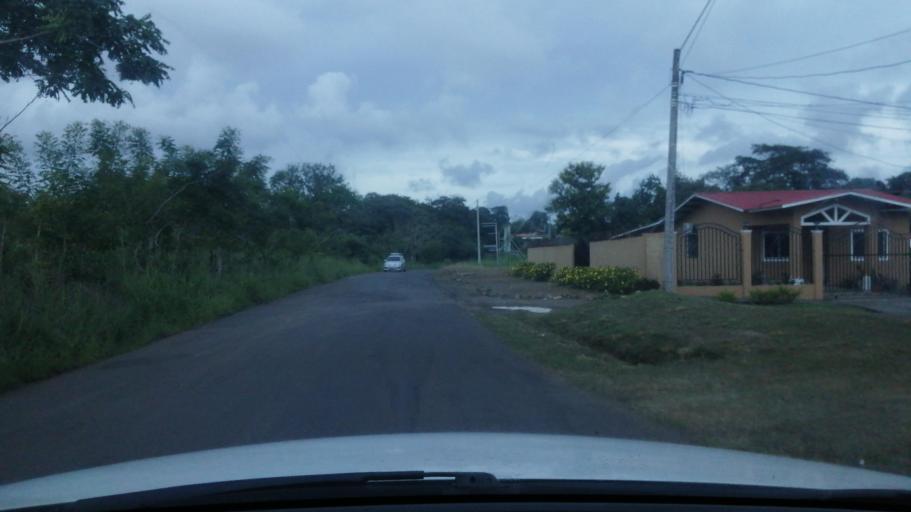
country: PA
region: Chiriqui
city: David
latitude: 8.4026
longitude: -82.4467
